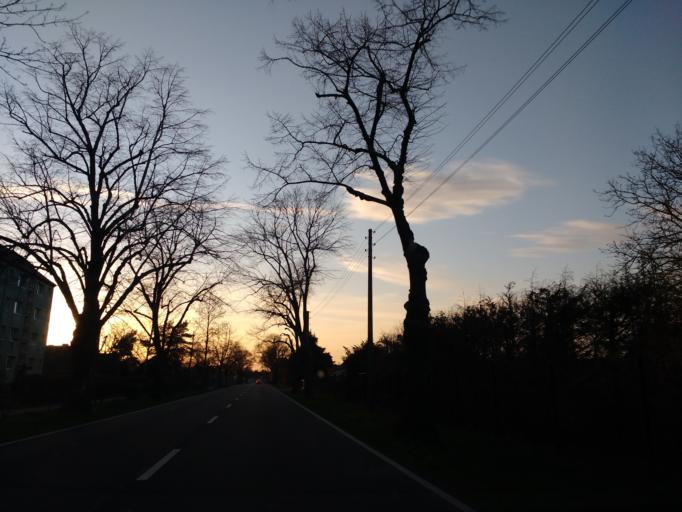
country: DE
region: Saxony-Anhalt
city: Zorbig
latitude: 51.6266
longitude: 12.1297
